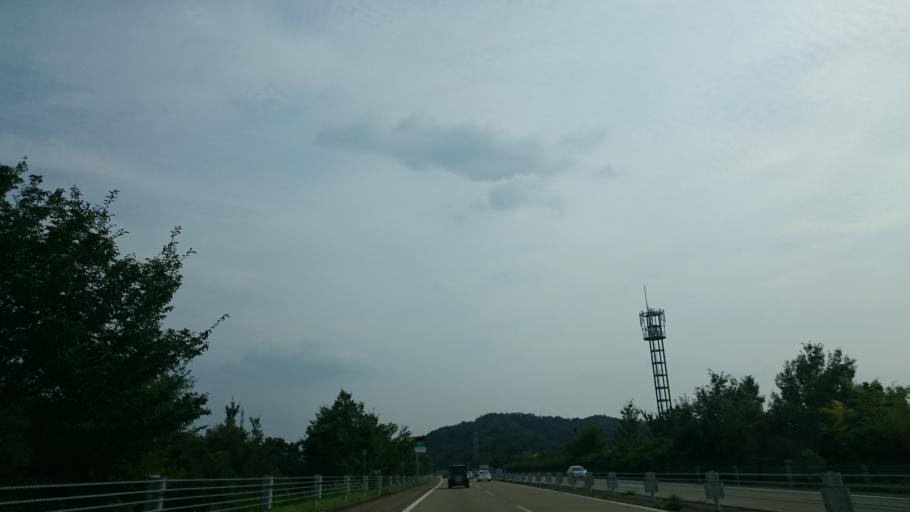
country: JP
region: Gifu
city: Mino
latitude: 35.4972
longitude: 136.8973
